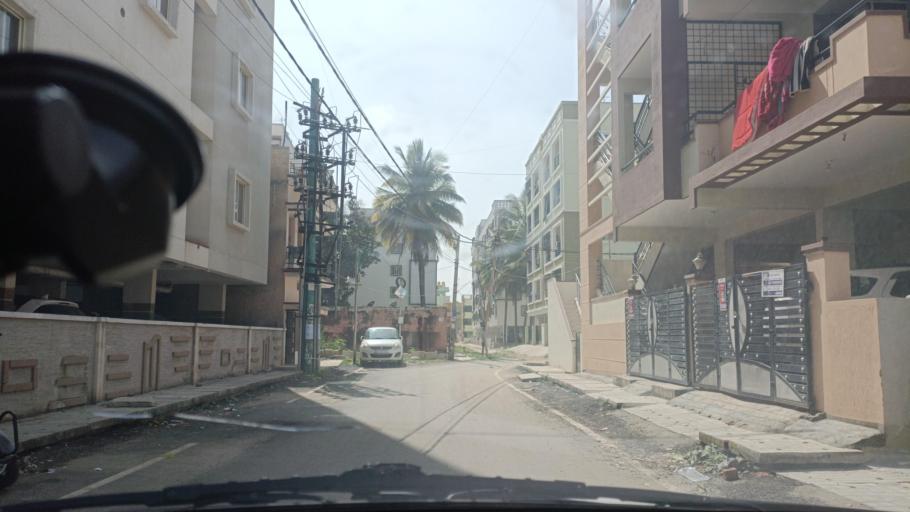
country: IN
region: Karnataka
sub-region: Bangalore Urban
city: Yelahanka
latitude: 13.1197
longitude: 77.6150
